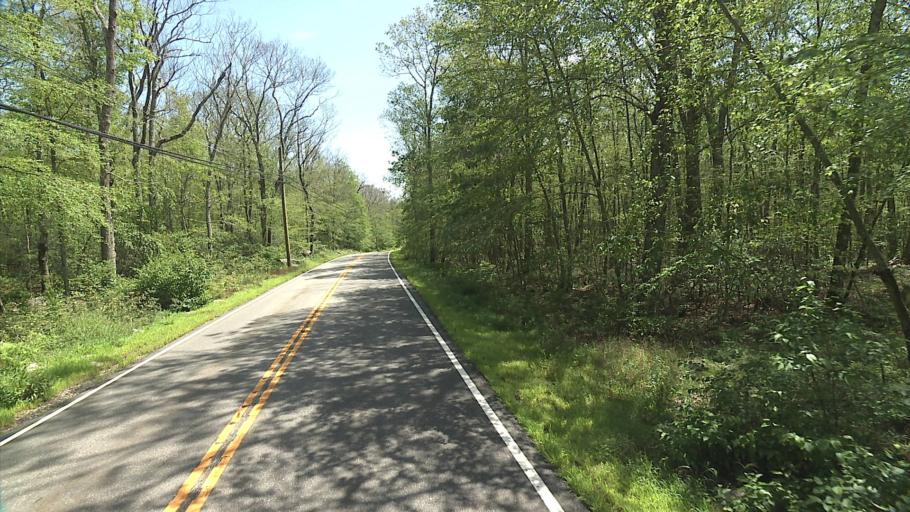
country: US
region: Connecticut
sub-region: Windham County
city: South Woodstock
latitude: 41.8986
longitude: -72.0207
